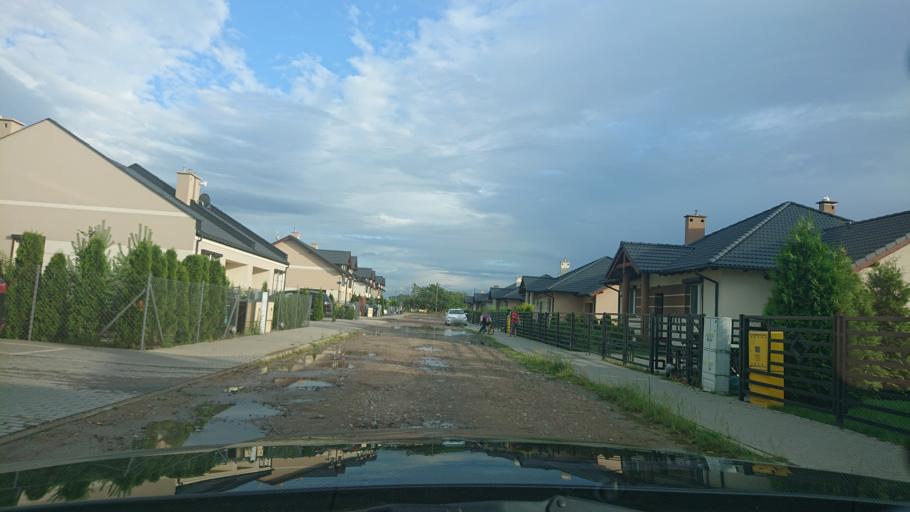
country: PL
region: Greater Poland Voivodeship
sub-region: Powiat gnieznienski
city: Gniezno
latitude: 52.5678
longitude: 17.6148
